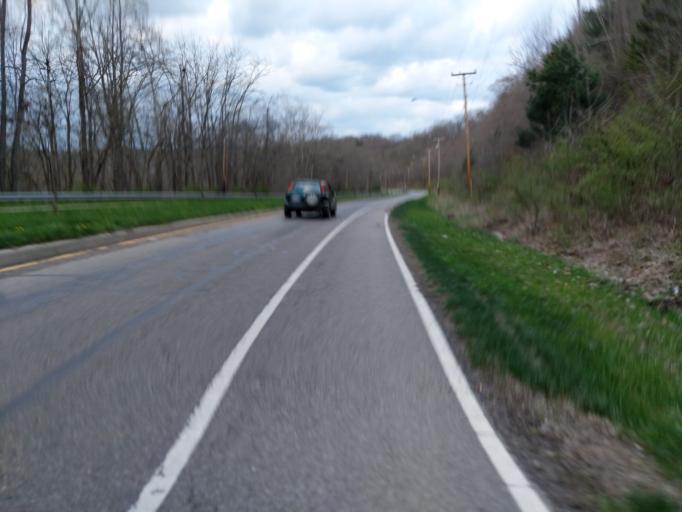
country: US
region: Ohio
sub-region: Athens County
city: Athens
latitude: 39.3408
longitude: -82.1021
